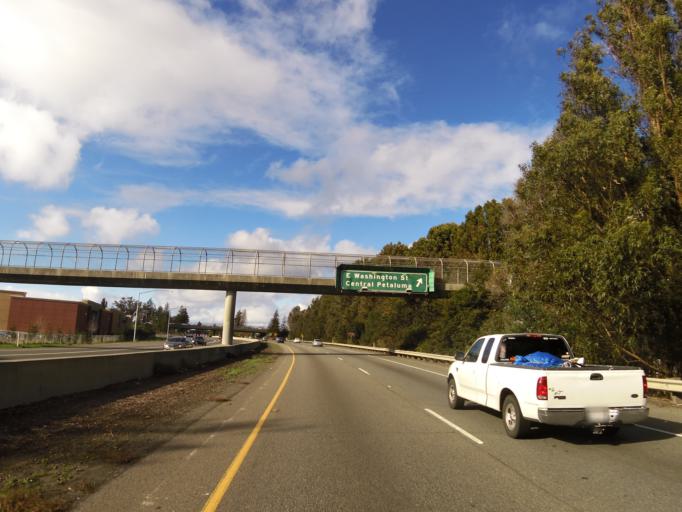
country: US
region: California
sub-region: Sonoma County
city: Petaluma
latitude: 38.2447
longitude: -122.6242
